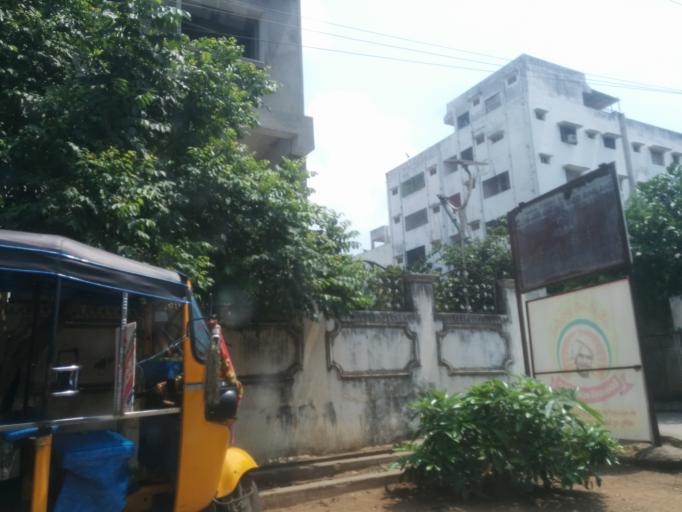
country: IN
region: Andhra Pradesh
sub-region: East Godavari
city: Rajahmundry
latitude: 17.0146
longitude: 81.7770
